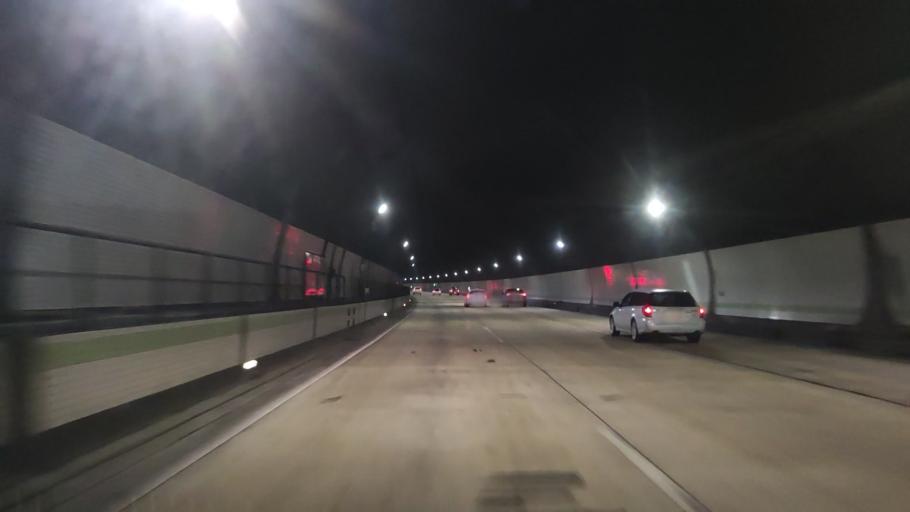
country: JP
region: Hyogo
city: Akashi
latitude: 34.6389
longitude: 135.0420
